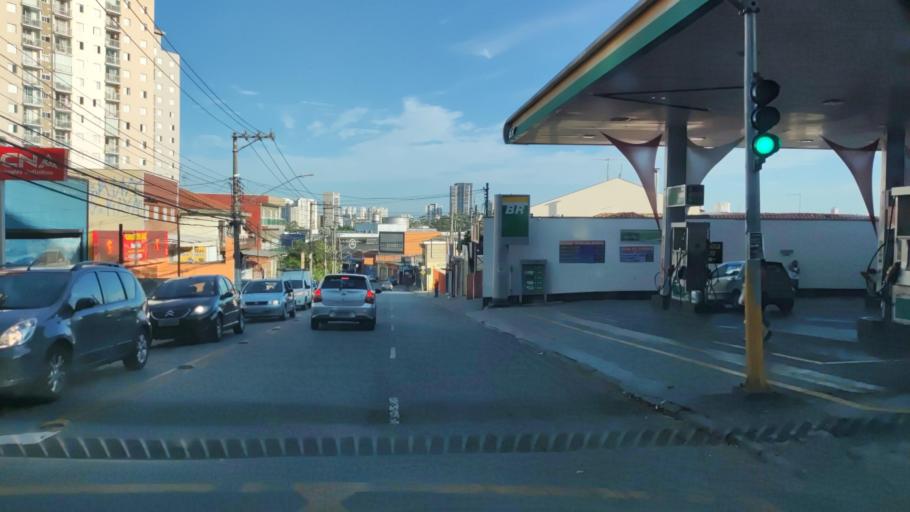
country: BR
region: Sao Paulo
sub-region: Osasco
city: Osasco
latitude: -23.5199
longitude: -46.7529
